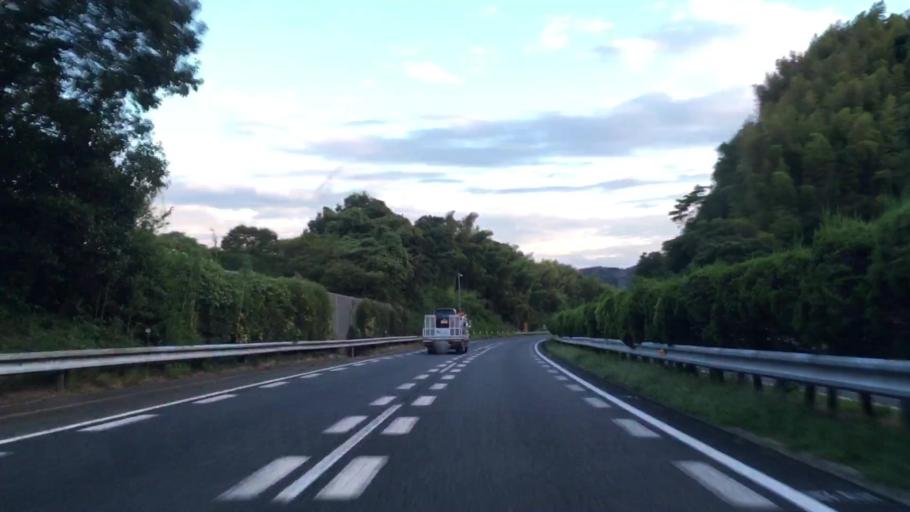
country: JP
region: Yamaguchi
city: Shimonoseki
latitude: 33.9359
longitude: 130.9962
